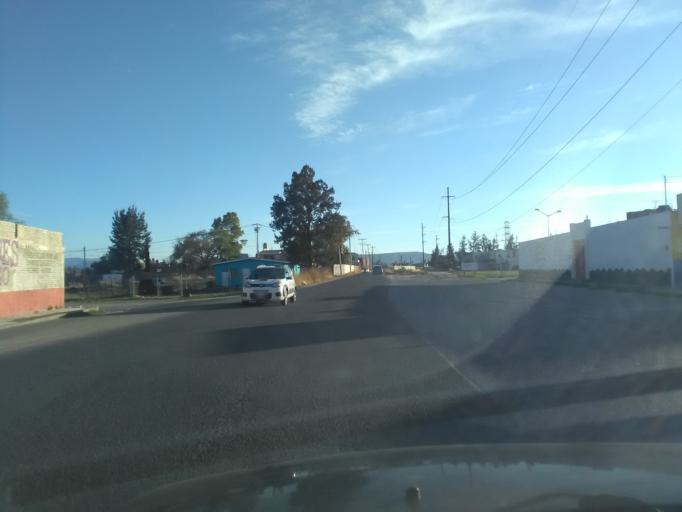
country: MX
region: Durango
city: Victoria de Durango
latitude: 24.0067
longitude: -104.6323
